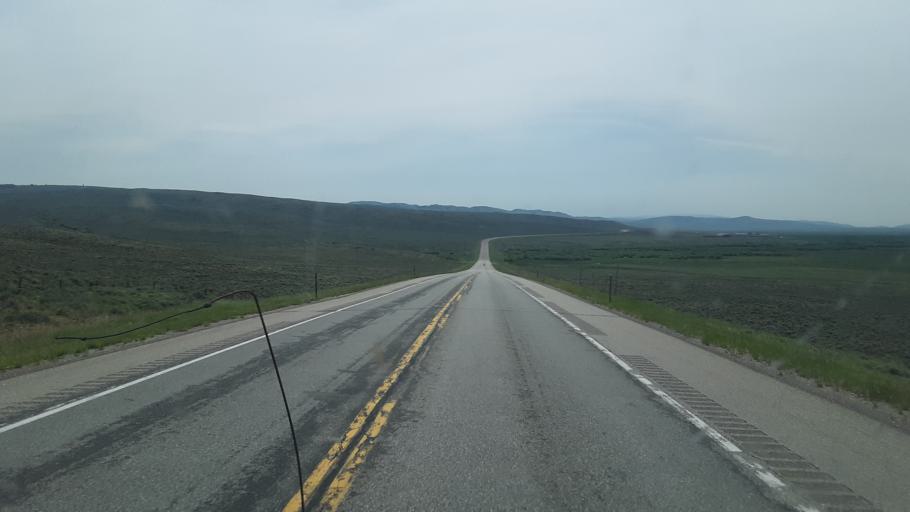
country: US
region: Colorado
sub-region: Jackson County
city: Walden
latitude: 41.0992
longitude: -106.5094
